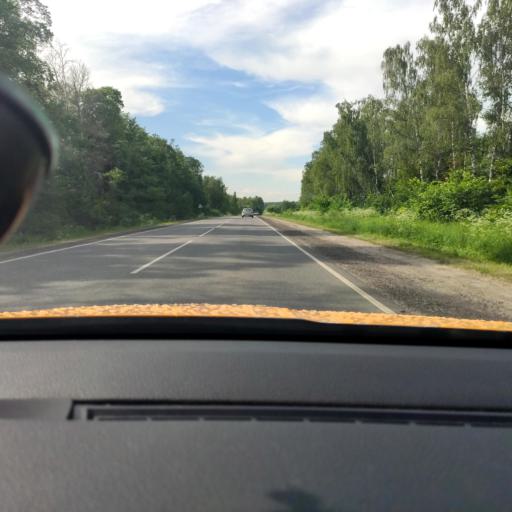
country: RU
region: Moskovskaya
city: Zhilevo
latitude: 54.9545
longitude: 38.0006
